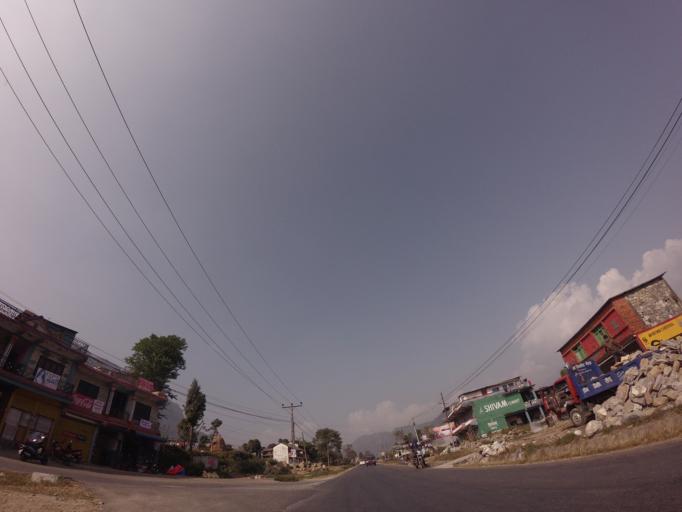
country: NP
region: Western Region
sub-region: Gandaki Zone
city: Pokhara
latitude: 28.2731
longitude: 83.9431
